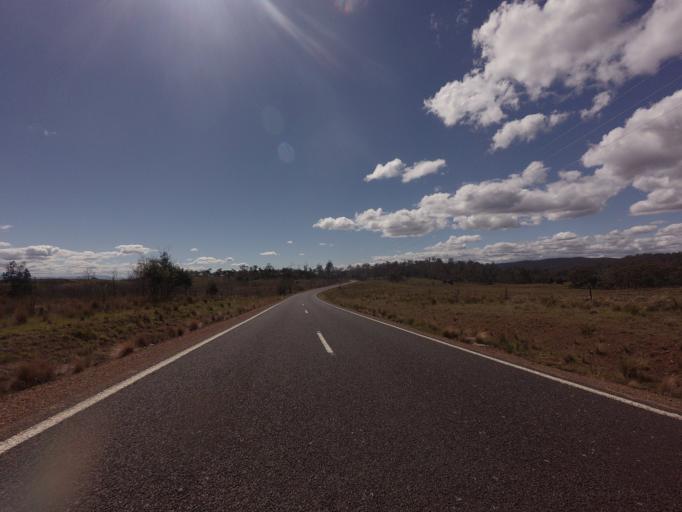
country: AU
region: Tasmania
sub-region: Northern Midlands
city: Evandale
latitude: -41.9560
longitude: 147.6129
